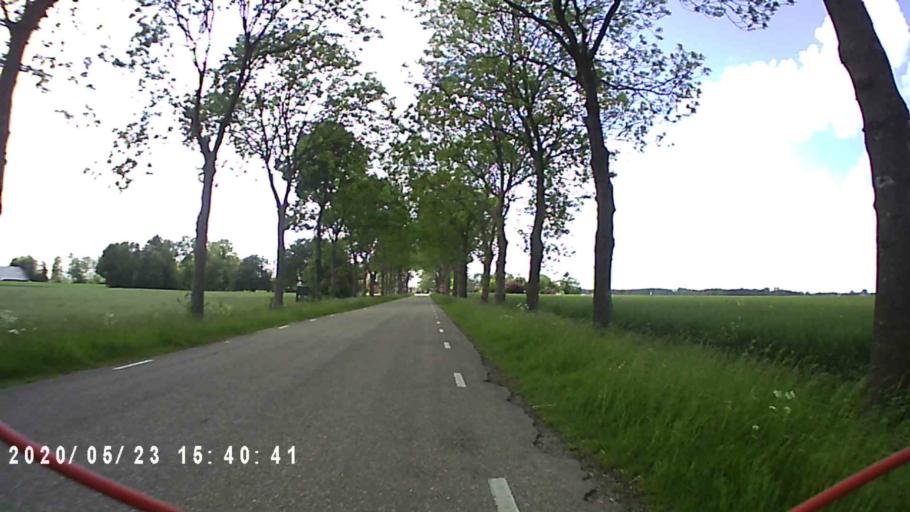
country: NL
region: Groningen
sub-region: Gemeente Delfzijl
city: Delfzijl
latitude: 53.2808
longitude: 6.9405
